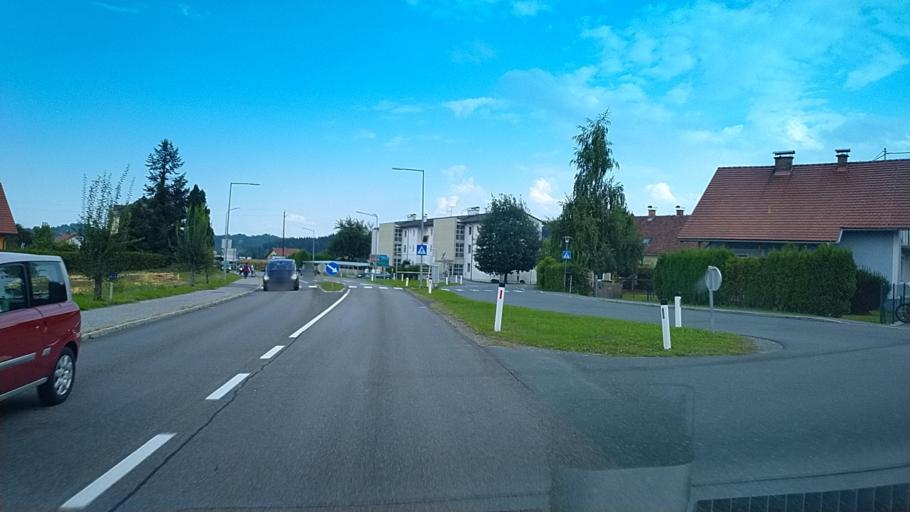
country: AT
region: Styria
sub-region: Politischer Bezirk Deutschlandsberg
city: Schwanberg
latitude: 46.7558
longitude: 15.2084
